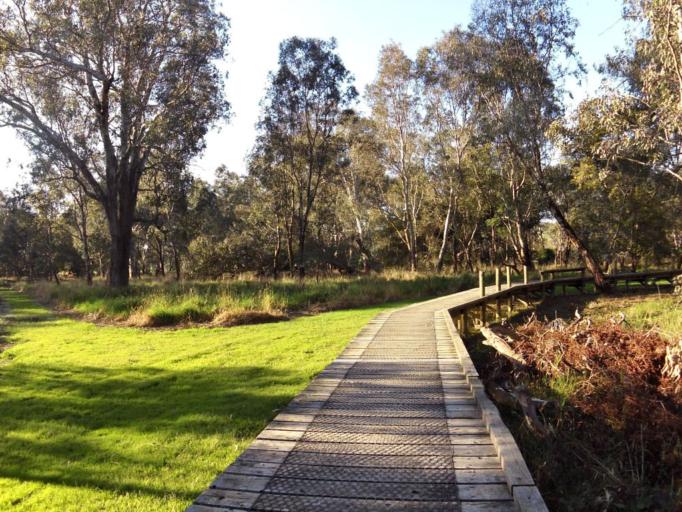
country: AU
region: Victoria
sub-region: Murrindindi
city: Alexandra
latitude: -37.2068
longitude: 145.4271
